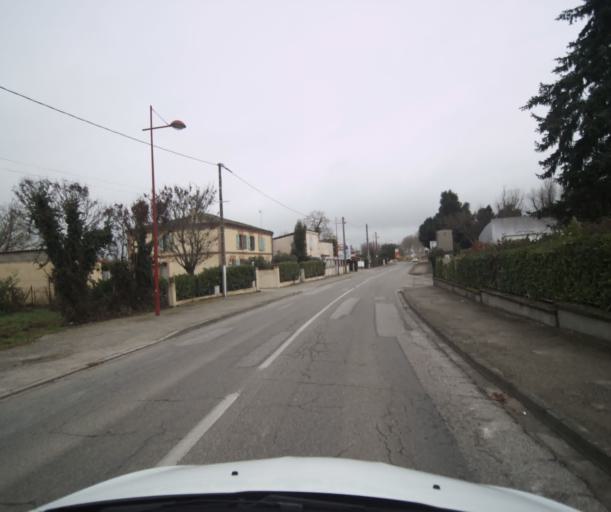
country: FR
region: Midi-Pyrenees
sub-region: Departement du Tarn-et-Garonne
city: Castelsarrasin
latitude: 44.0439
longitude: 1.1133
